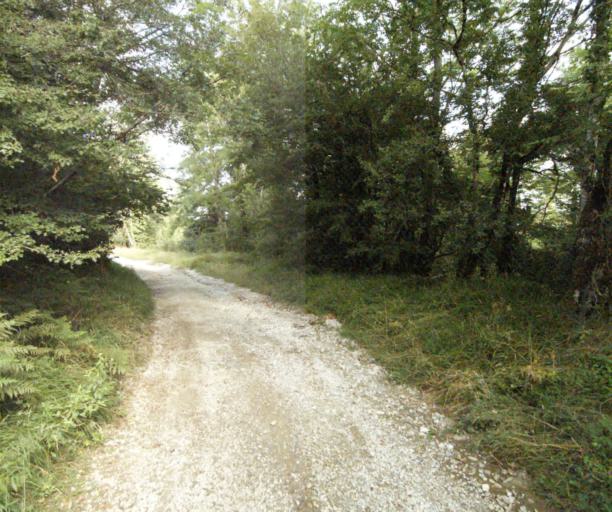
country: FR
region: Midi-Pyrenees
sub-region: Departement du Tarn
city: Dourgne
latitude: 43.4584
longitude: 2.1198
